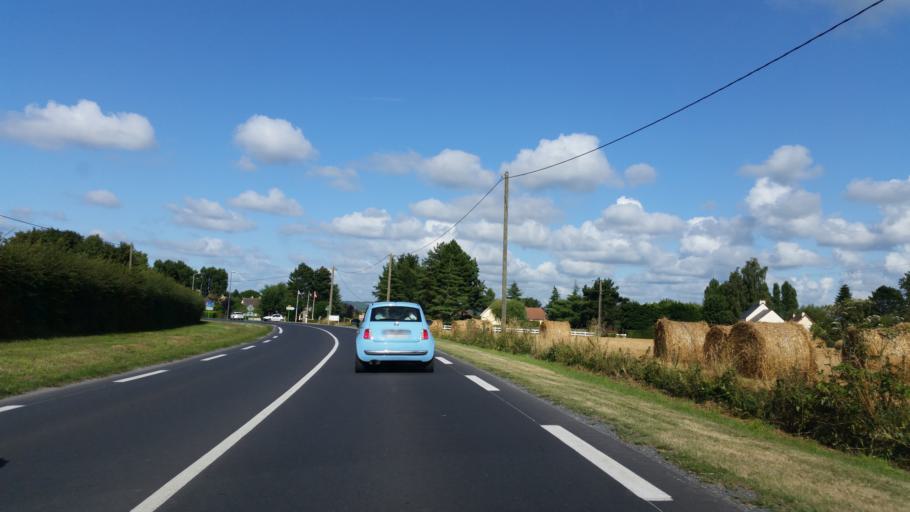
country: FR
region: Lower Normandy
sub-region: Departement du Calvados
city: Bavent
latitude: 49.2509
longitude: -0.1642
